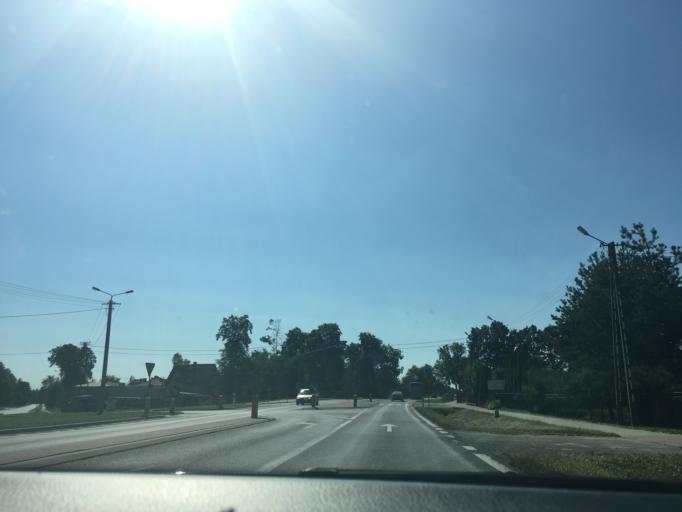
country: PL
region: Lublin Voivodeship
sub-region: Powiat lubartowski
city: Serniki
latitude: 51.4275
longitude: 22.6352
